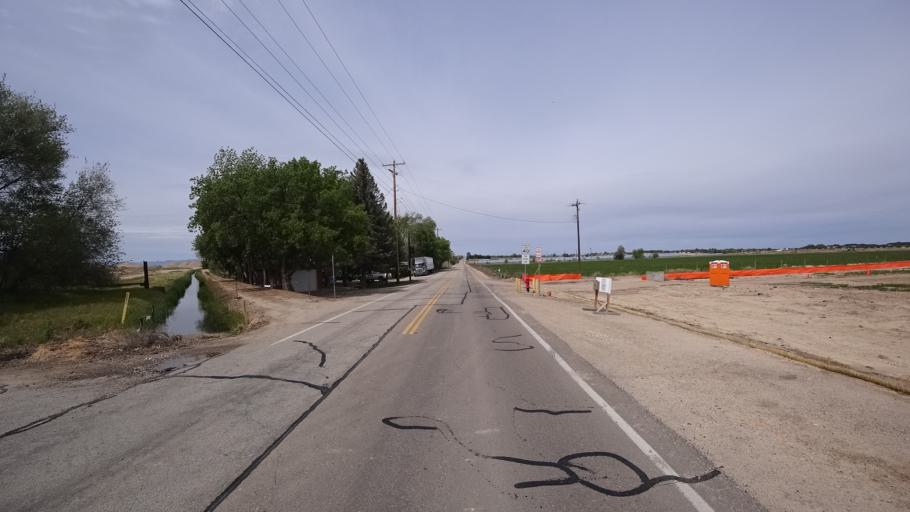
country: US
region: Idaho
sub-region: Ada County
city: Meridian
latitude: 43.5611
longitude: -116.3819
